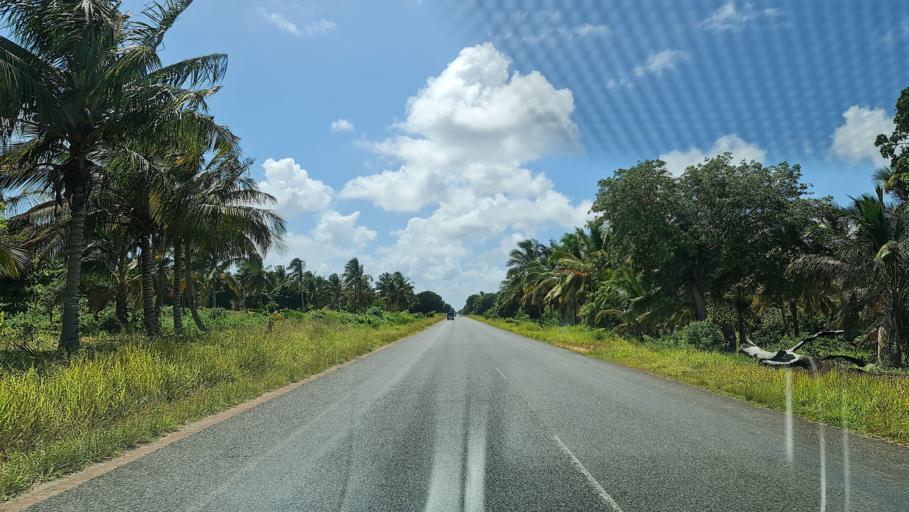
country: MZ
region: Inhambane
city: Maxixe
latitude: -24.5420
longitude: 34.9042
